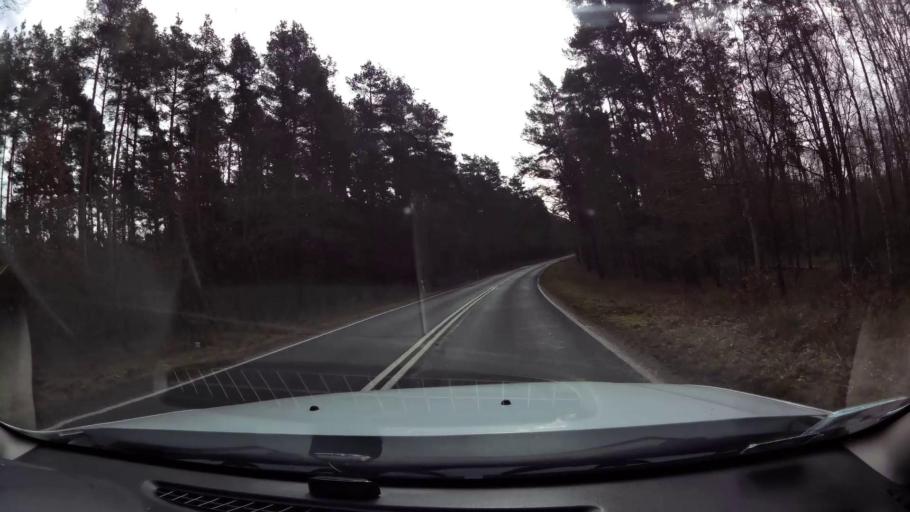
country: PL
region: West Pomeranian Voivodeship
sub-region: Powiat mysliborski
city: Debno
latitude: 52.7666
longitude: 14.6757
